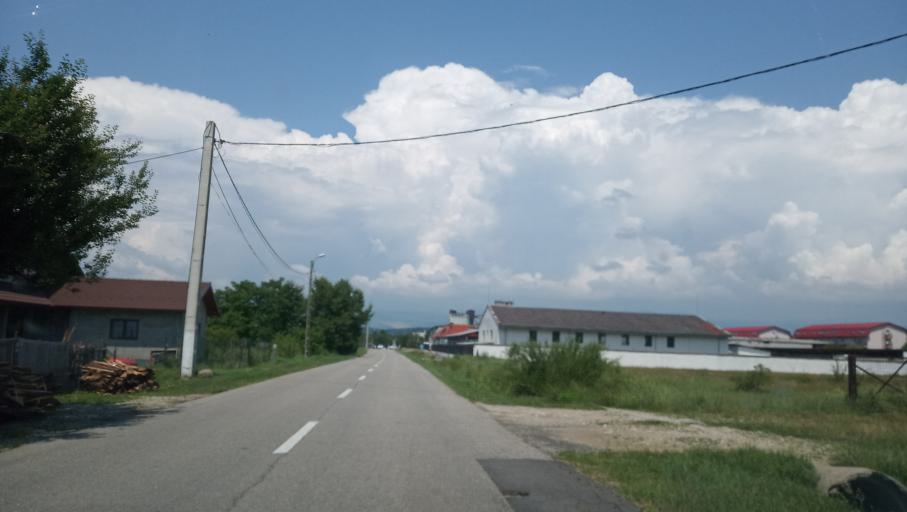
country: RO
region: Gorj
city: Targu Jiu
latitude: 45.0659
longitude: 23.3140
